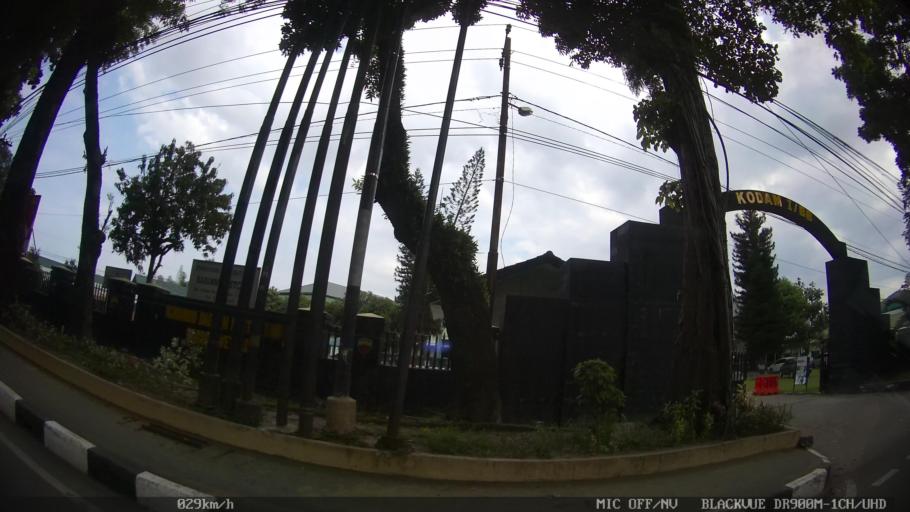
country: ID
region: North Sumatra
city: Medan
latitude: 3.5802
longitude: 98.6802
